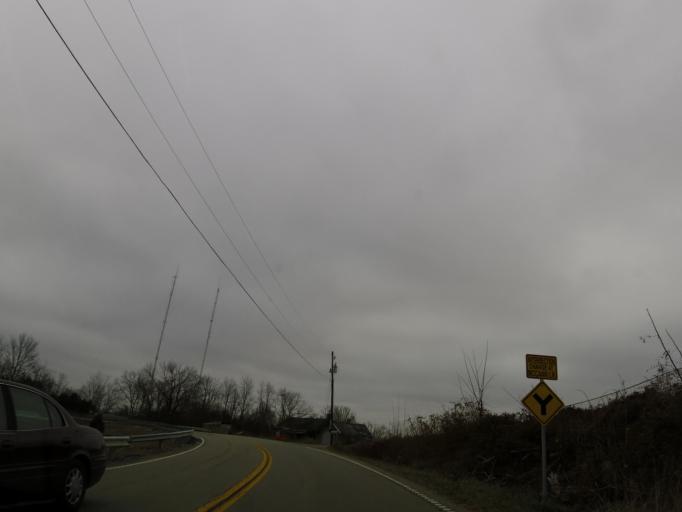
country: US
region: Kentucky
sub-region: Franklin County
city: Frankfort
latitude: 38.2179
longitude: -84.9089
